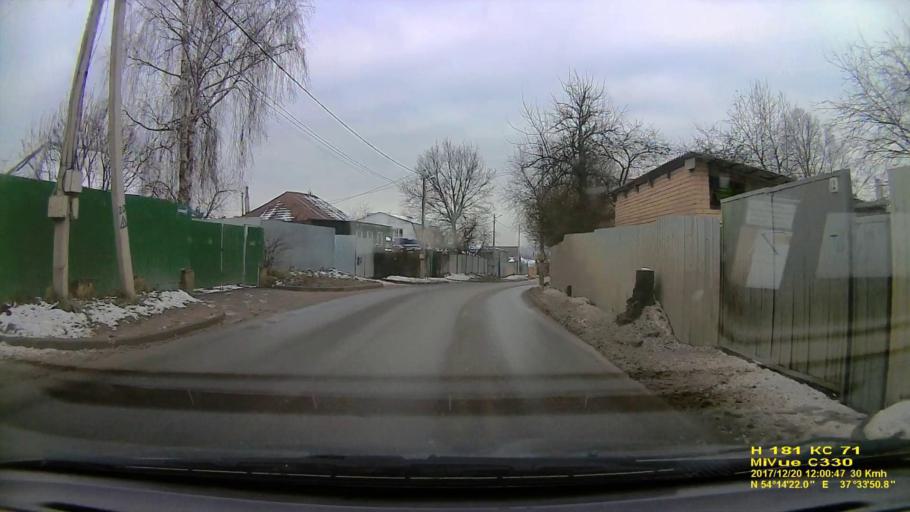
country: RU
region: Tula
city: Gorelki
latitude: 54.2394
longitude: 37.5642
